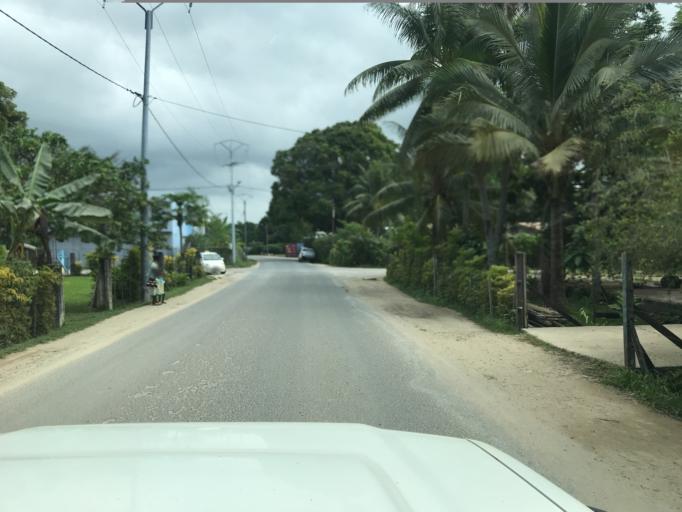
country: VU
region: Sanma
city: Luganville
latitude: -15.5123
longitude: 167.1719
